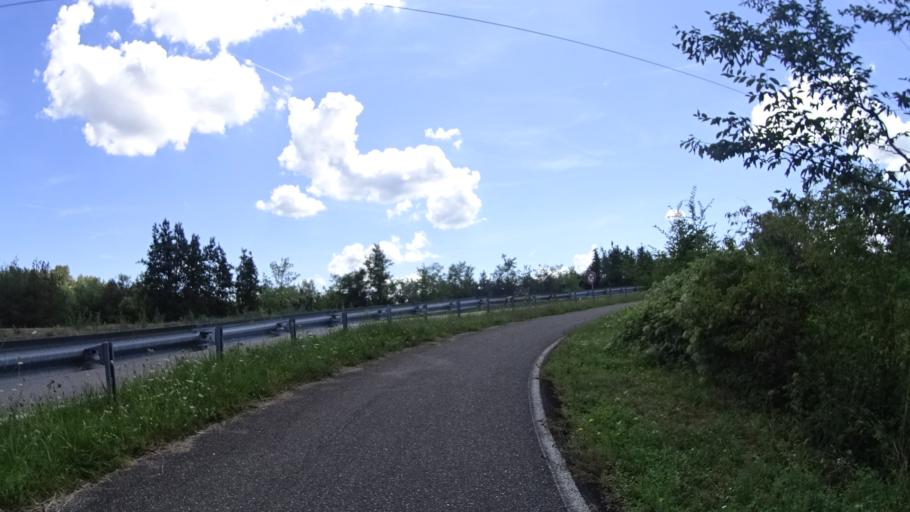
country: FR
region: Alsace
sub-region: Departement du Haut-Rhin
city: Habsheim
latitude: 47.7648
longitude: 7.4482
